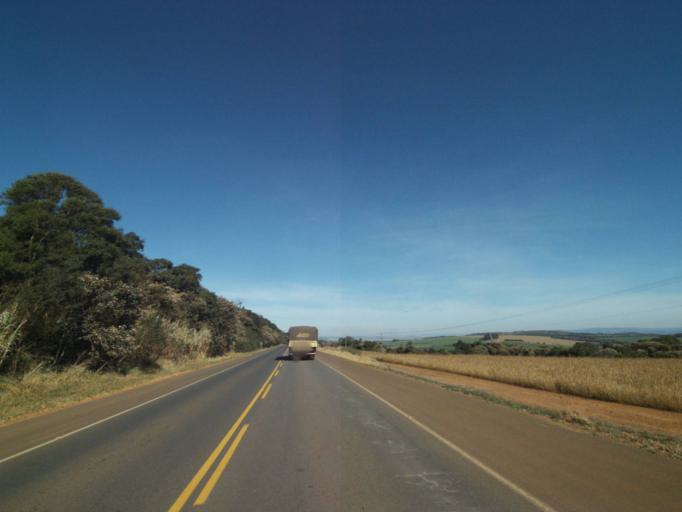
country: BR
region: Parana
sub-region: Tibagi
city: Tibagi
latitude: -24.3716
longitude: -50.3265
